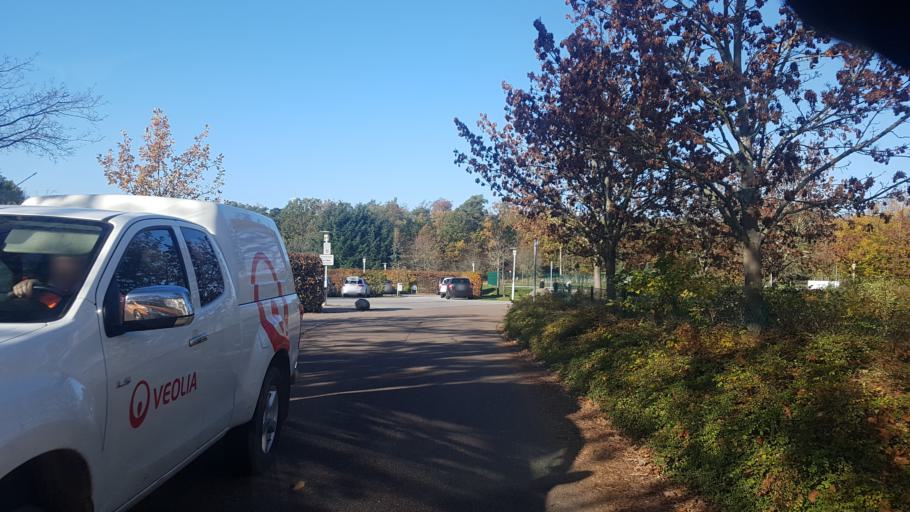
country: DE
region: Saxony
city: Dahlen
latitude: 51.3991
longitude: 12.9943
